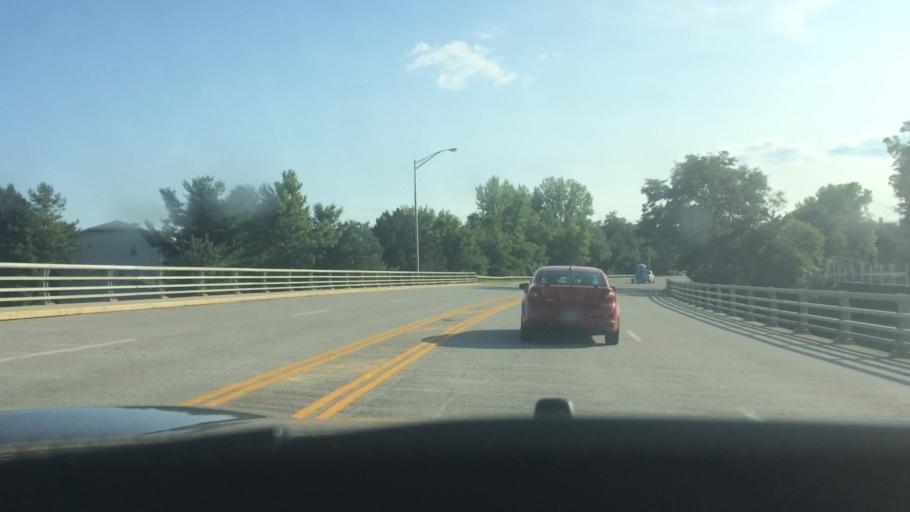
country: US
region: New York
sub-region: St. Lawrence County
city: Potsdam
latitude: 44.6697
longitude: -74.9914
